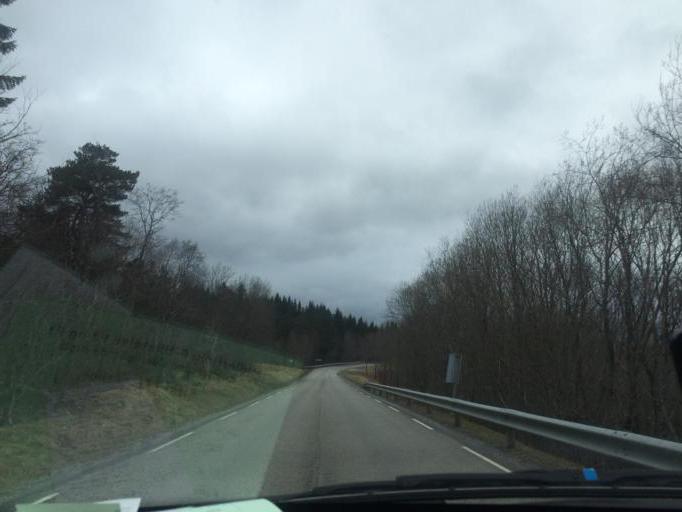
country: NO
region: More og Romsdal
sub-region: Gjemnes
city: Batnfjordsora
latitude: 62.9645
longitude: 7.7453
